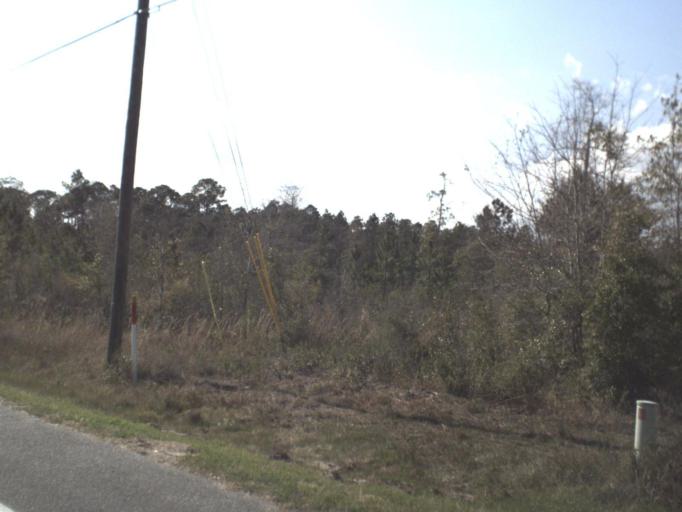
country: US
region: Florida
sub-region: Wakulla County
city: Crawfordville
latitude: 30.0665
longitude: -84.4636
